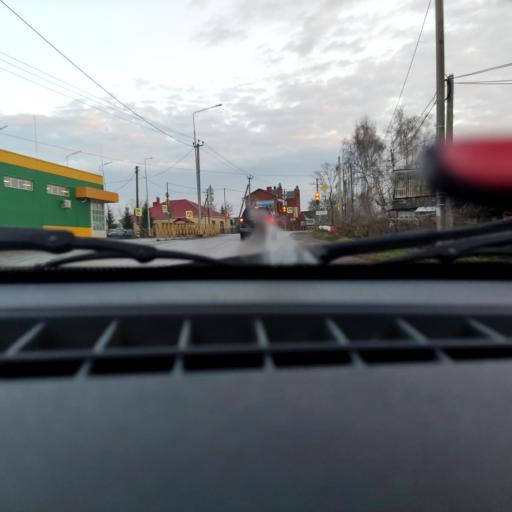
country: RU
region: Bashkortostan
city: Avdon
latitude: 54.4989
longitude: 55.8839
